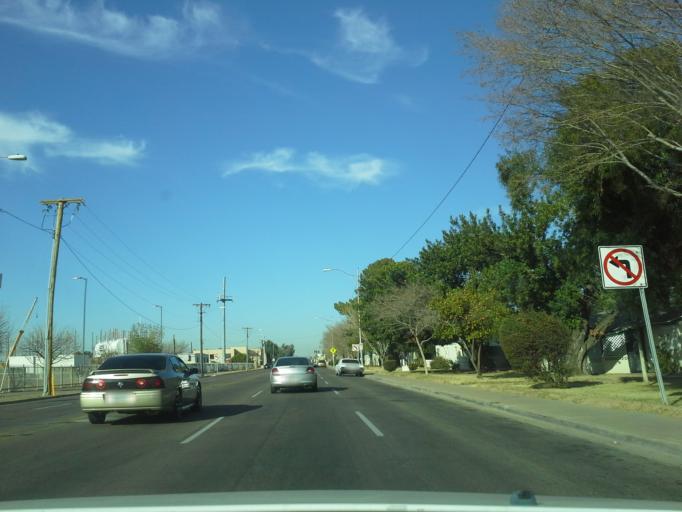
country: US
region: Arizona
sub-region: Maricopa County
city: Phoenix
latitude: 33.4819
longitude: -112.0999
